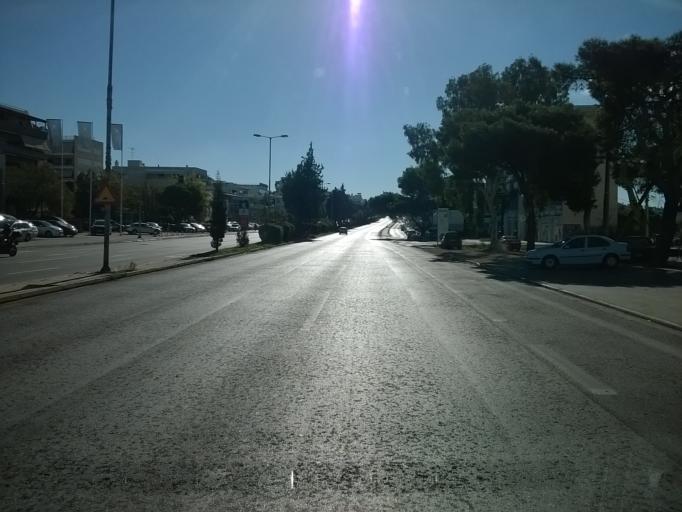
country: GR
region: Attica
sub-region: Nomarchia Athinas
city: Glyfada
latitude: 37.8601
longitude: 23.7635
